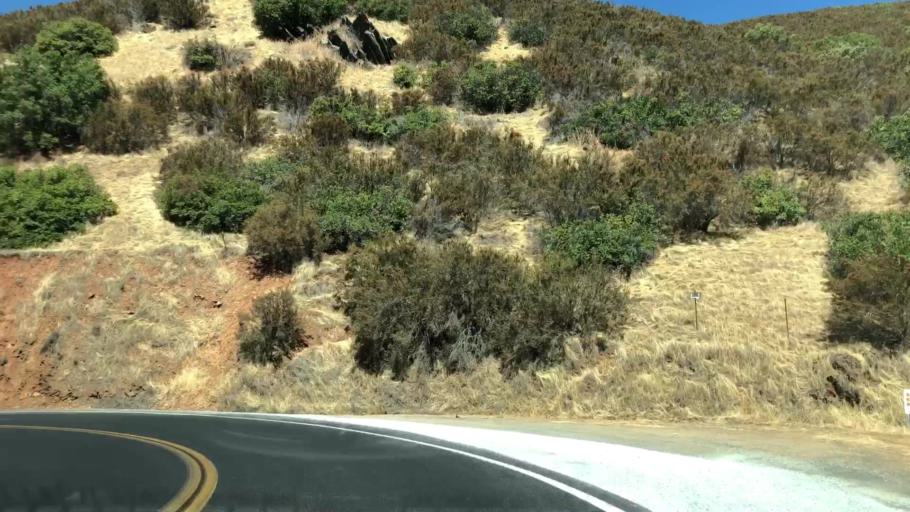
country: US
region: California
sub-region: Tuolumne County
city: Tuolumne City
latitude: 37.8199
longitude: -120.2961
